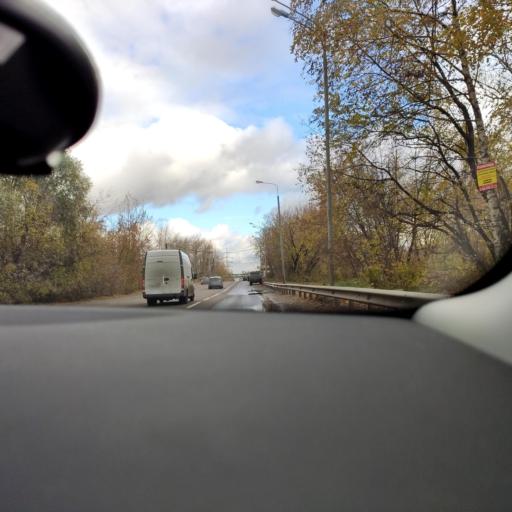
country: RU
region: Moskovskaya
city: Kotel'niki
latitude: 55.6474
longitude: 37.8442
